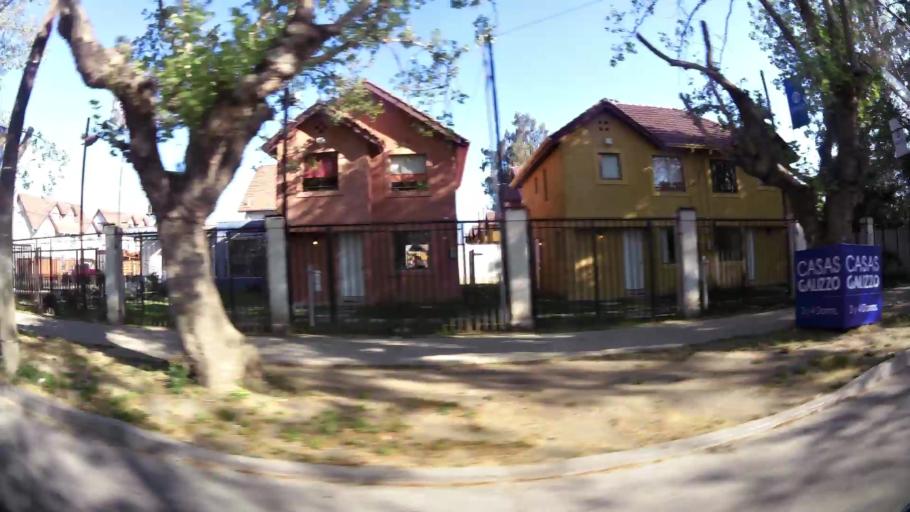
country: CL
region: Santiago Metropolitan
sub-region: Provincia de Talagante
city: Penaflor
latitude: -33.6101
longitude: -70.8638
